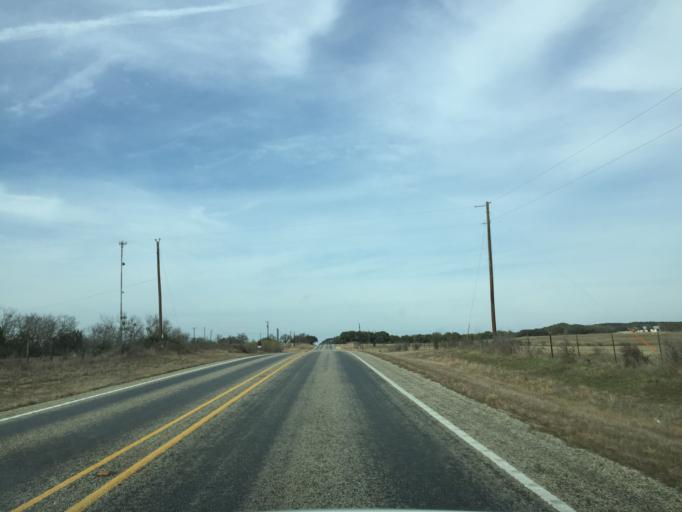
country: US
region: Texas
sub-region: Gillespie County
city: Fredericksburg
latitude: 30.4312
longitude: -98.7371
